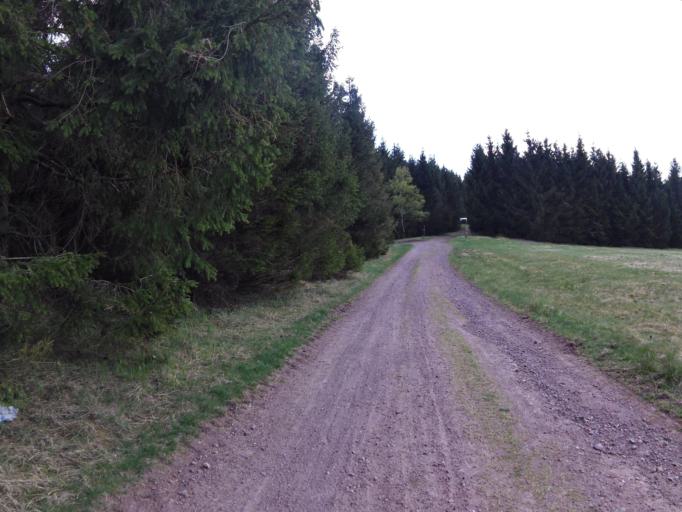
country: DE
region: Thuringia
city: Unterschonau
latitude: 50.7574
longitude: 10.5645
